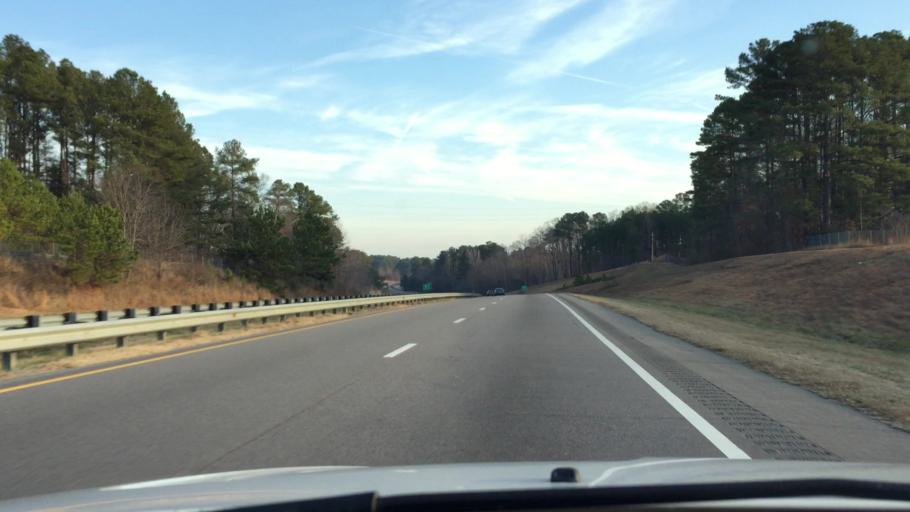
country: US
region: North Carolina
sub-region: Lee County
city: Sanford
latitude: 35.4594
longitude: -79.2075
